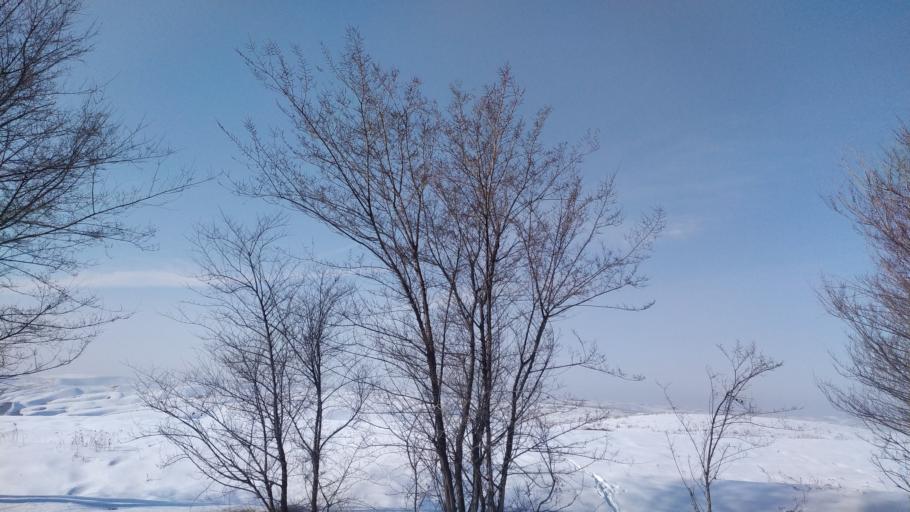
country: KZ
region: Almaty Oblysy
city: Burunday
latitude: 43.2602
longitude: 76.4704
